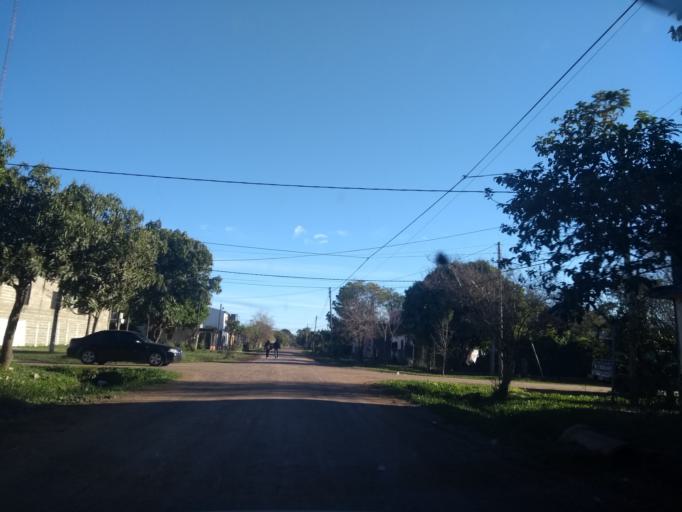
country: AR
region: Chaco
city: Barranqueras
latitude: -27.4772
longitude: -58.9316
